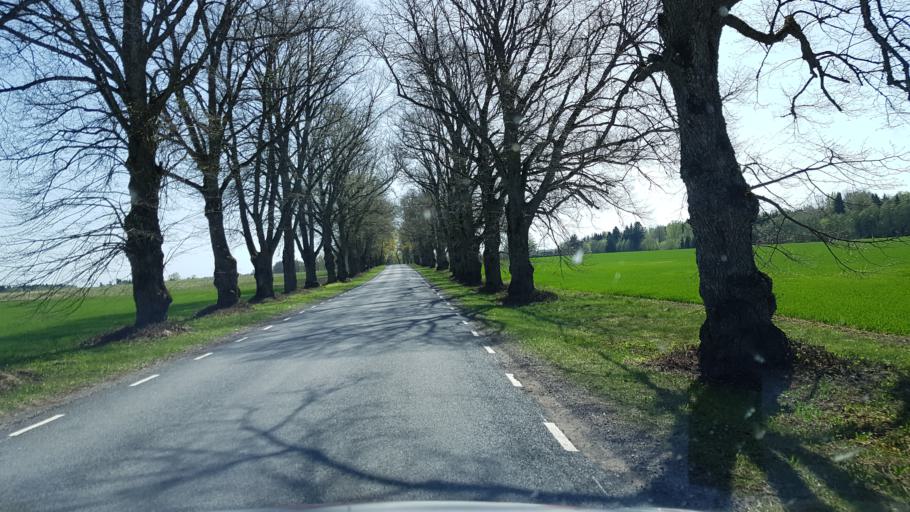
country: EE
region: Viljandimaa
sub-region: Vohma linn
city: Vohma
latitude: 58.5465
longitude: 25.5675
